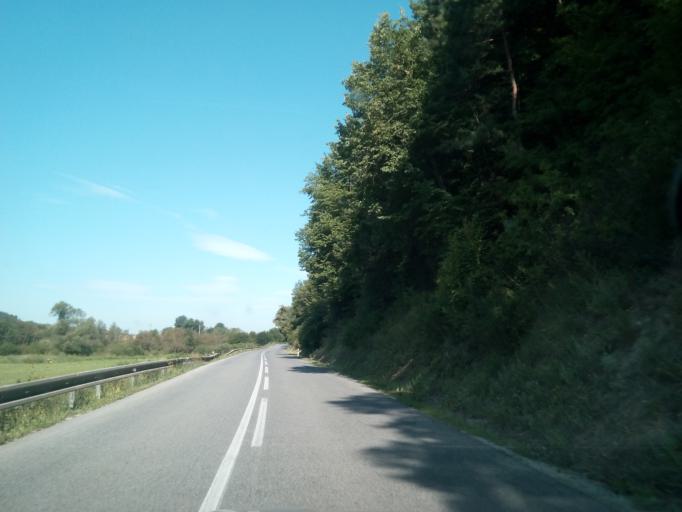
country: SK
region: Kosicky
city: Krompachy
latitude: 48.9359
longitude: 20.8347
